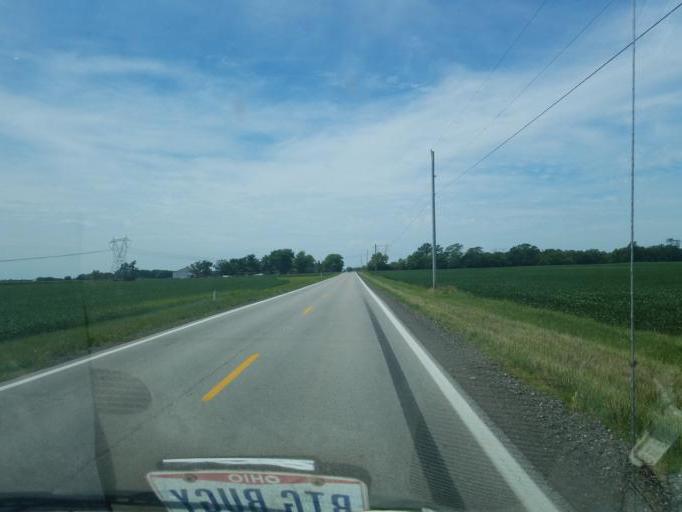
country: US
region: Ohio
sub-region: Madison County
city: West Jefferson
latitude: 39.8724
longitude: -83.2971
